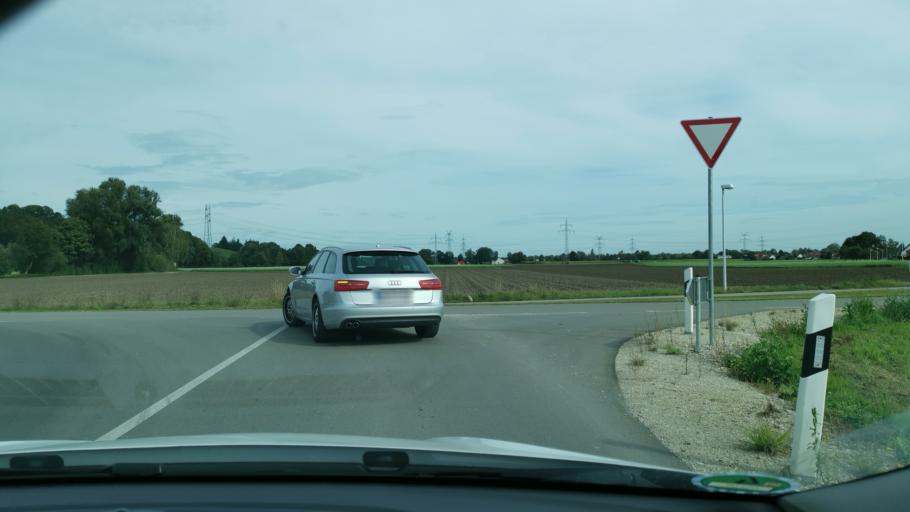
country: DE
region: Bavaria
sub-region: Upper Bavaria
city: Bergkirchen
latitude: 48.2509
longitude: 11.3640
